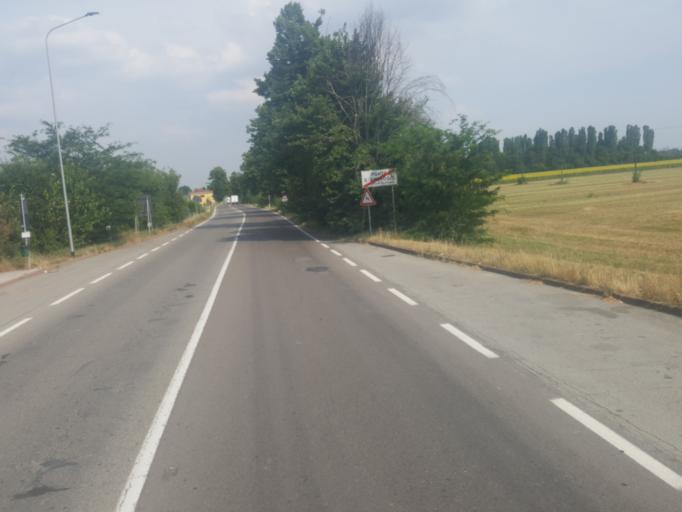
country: IT
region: Emilia-Romagna
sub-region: Provincia di Modena
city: Gaggio
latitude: 44.6208
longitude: 11.0068
